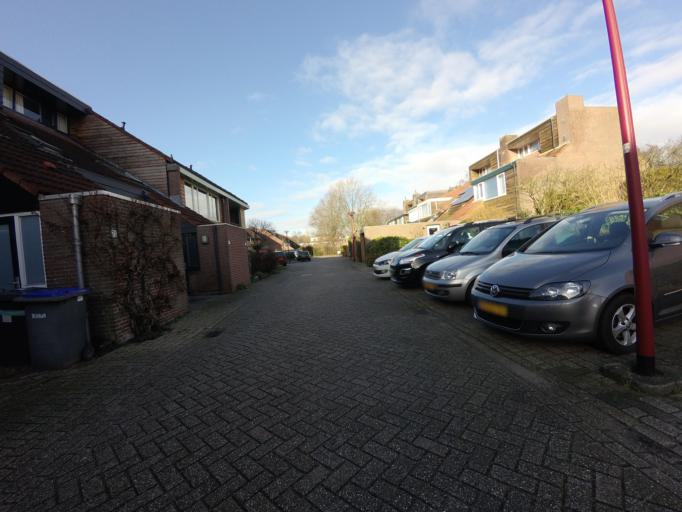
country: NL
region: Utrecht
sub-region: Gemeente Nieuwegein
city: Nieuwegein
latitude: 52.0434
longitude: 5.0722
